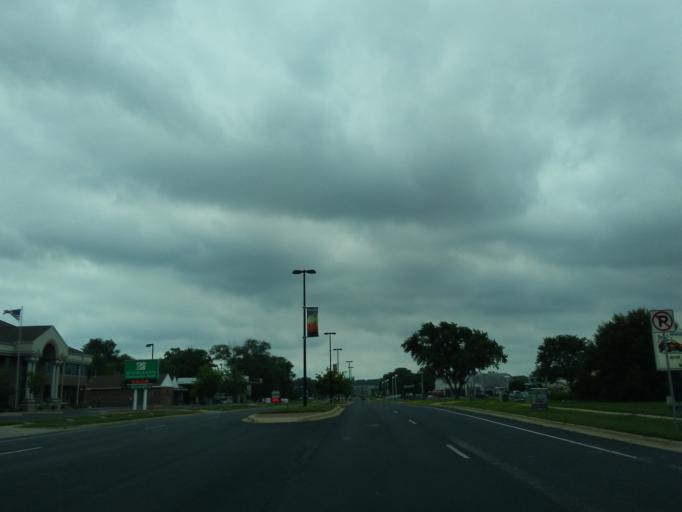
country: US
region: Wisconsin
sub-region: Dane County
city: Middleton
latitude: 43.1101
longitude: -89.5098
